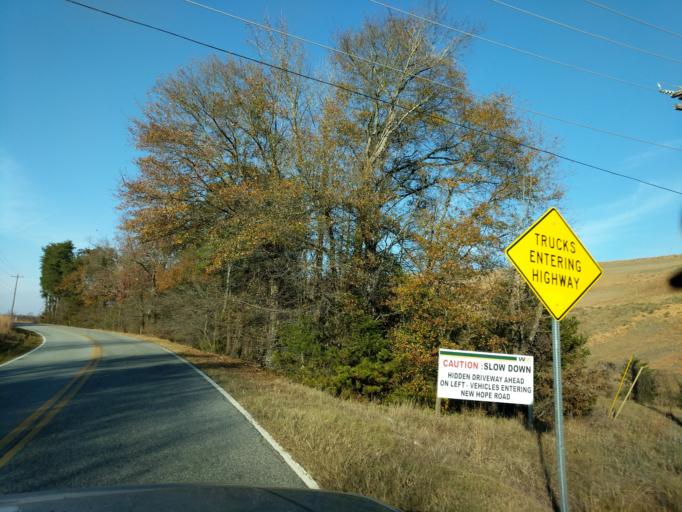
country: US
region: South Carolina
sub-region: Spartanburg County
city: Wellford
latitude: 34.9270
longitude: -82.0784
